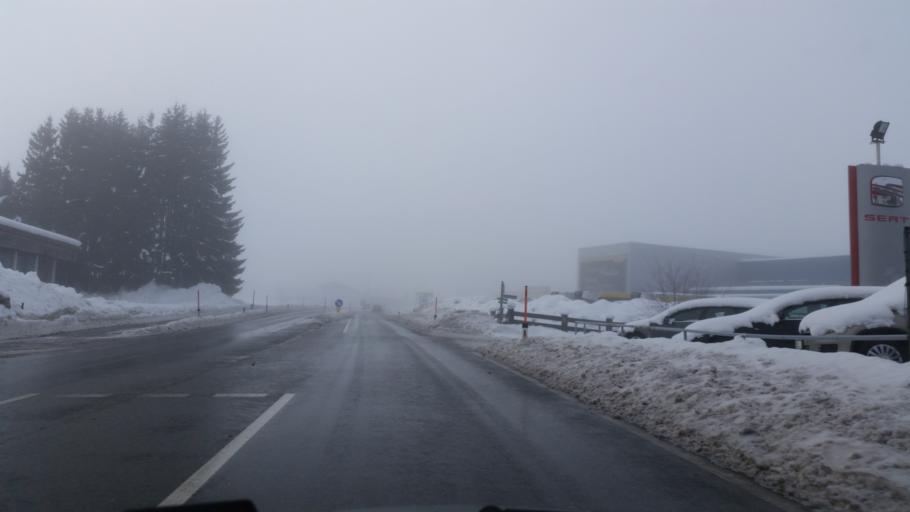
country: AT
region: Tyrol
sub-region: Politischer Bezirk Kitzbuhel
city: Kirchdorf in Tirol
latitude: 47.5404
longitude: 12.4445
